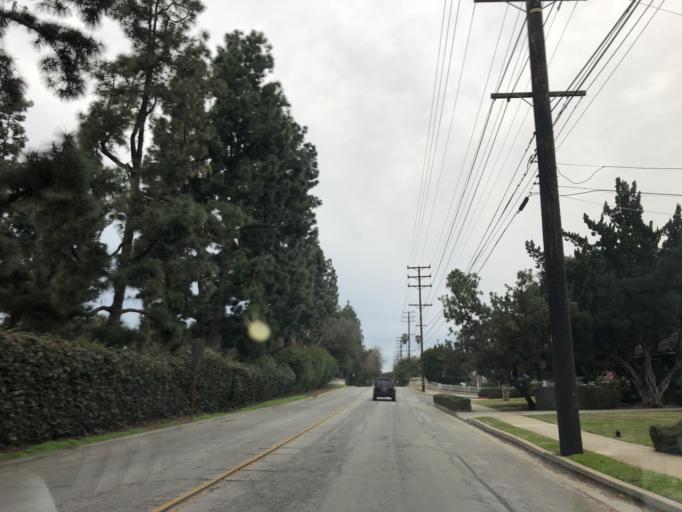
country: US
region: California
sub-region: Los Angeles County
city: San Marino
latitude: 34.1135
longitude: -118.0964
